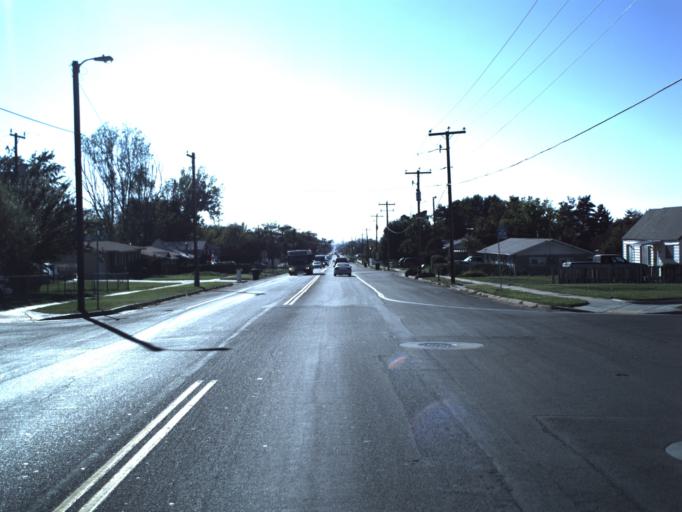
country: US
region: Utah
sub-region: Davis County
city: Sunset
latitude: 41.1399
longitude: -112.0362
